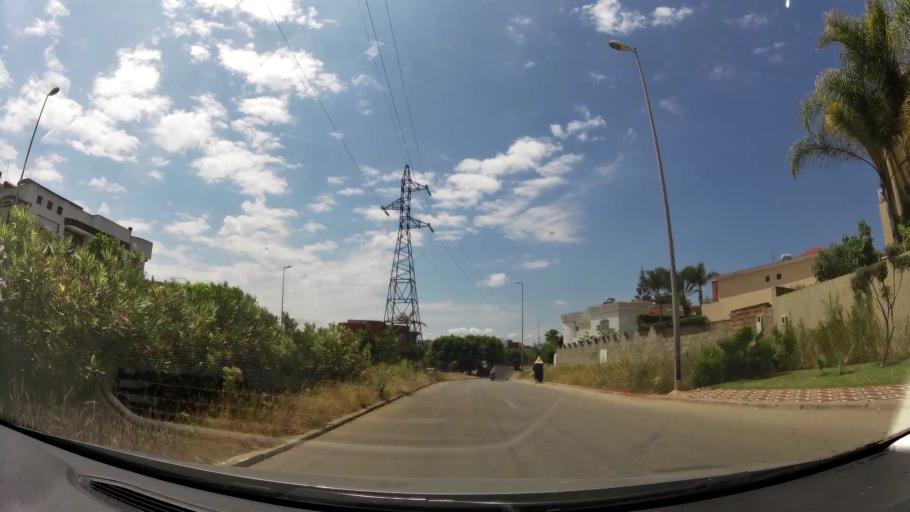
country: MA
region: Gharb-Chrarda-Beni Hssen
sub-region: Kenitra Province
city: Kenitra
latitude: 34.2715
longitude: -6.6138
